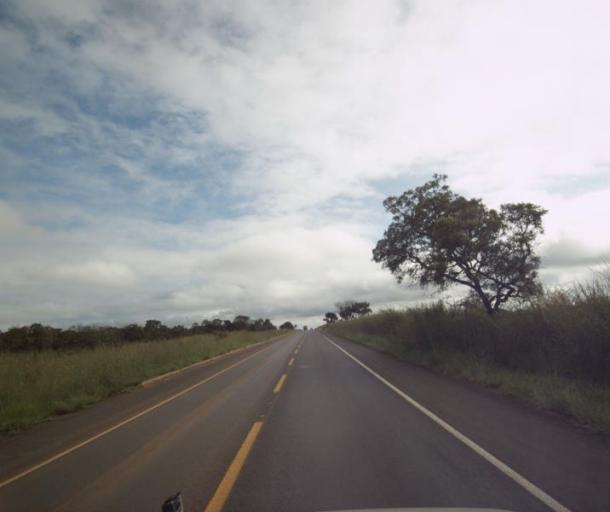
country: BR
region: Goias
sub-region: Padre Bernardo
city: Padre Bernardo
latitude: -15.3597
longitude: -48.6464
